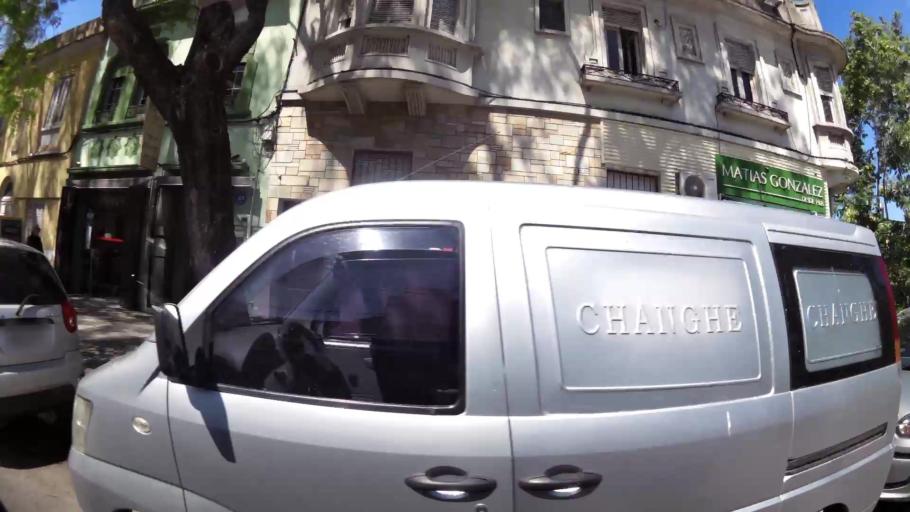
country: UY
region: Montevideo
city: Montevideo
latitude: -34.9151
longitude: -56.1561
